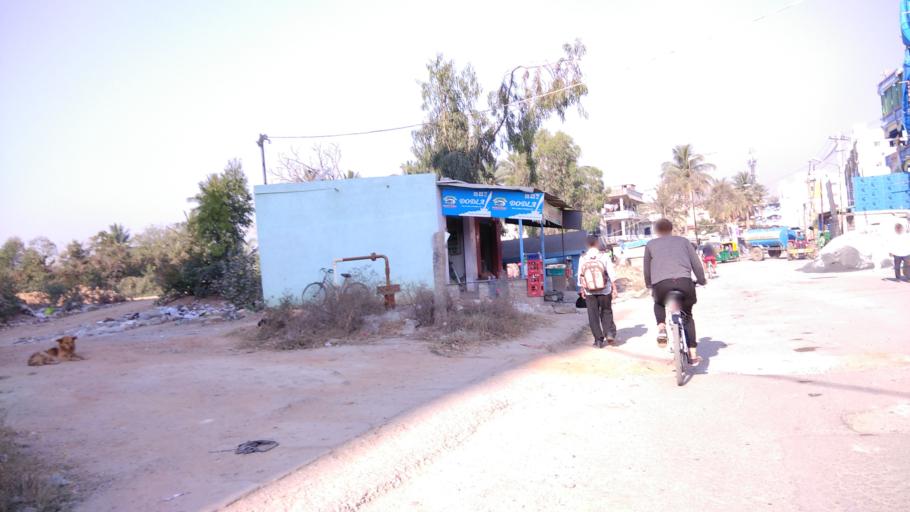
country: IN
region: Karnataka
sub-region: Bangalore Rural
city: Hoskote
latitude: 12.9777
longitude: 77.7375
